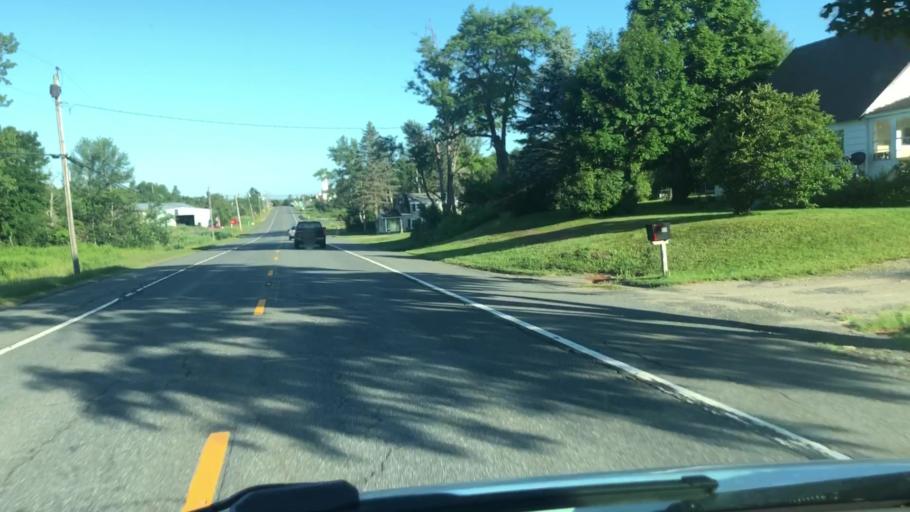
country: US
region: Massachusetts
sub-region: Berkshire County
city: Hinsdale
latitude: 42.5098
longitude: -73.0499
